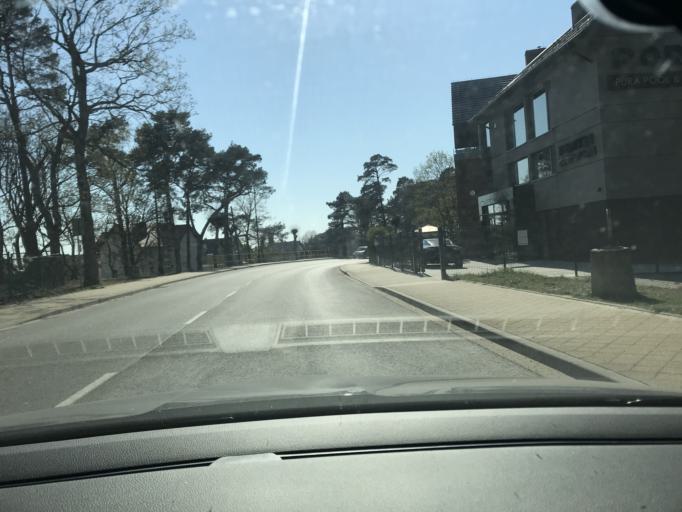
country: PL
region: Pomeranian Voivodeship
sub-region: Powiat nowodworski
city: Krynica Morska
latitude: 54.3772
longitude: 19.4352
